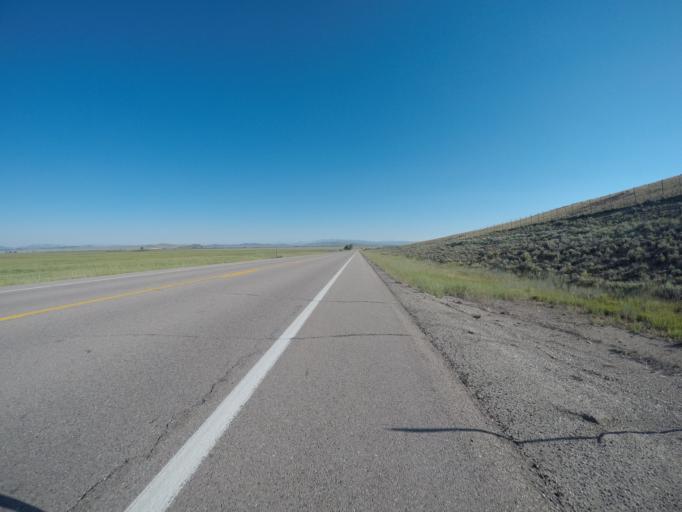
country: US
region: Wyoming
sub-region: Sublette County
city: Pinedale
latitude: 42.9465
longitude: -110.0846
